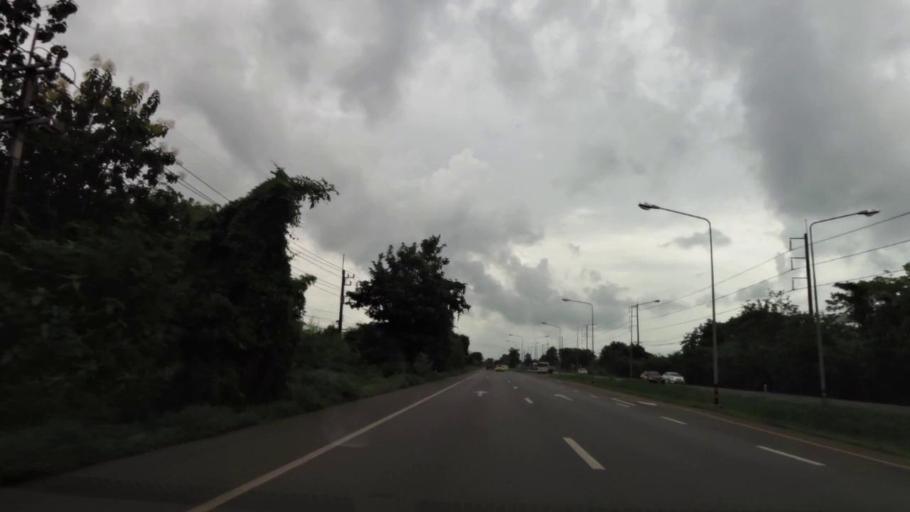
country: TH
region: Chanthaburi
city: Tha Mai
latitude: 12.6911
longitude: 101.9956
